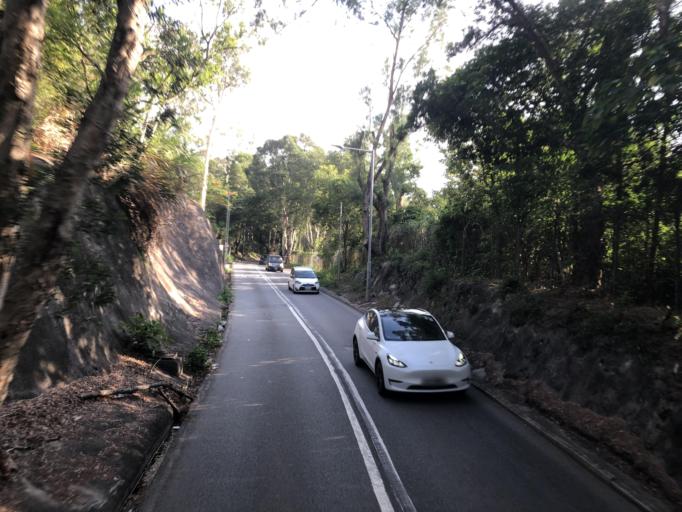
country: HK
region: Tai Po
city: Tai Po
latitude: 22.4936
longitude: 114.1199
